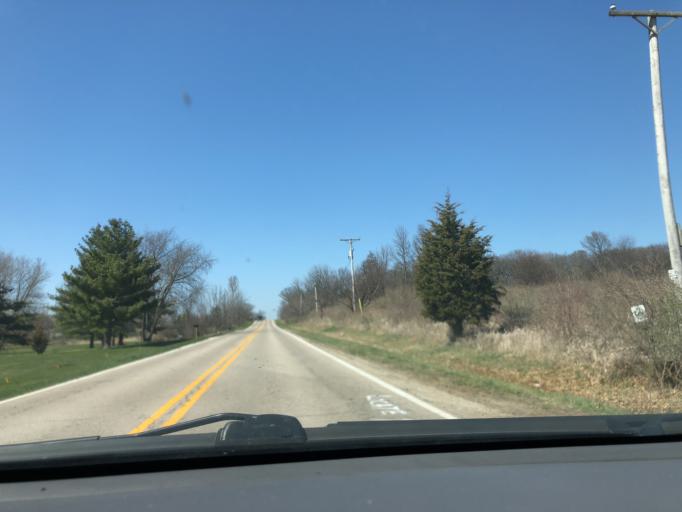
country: US
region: Illinois
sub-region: Kane County
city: Hampshire
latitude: 42.1083
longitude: -88.4911
